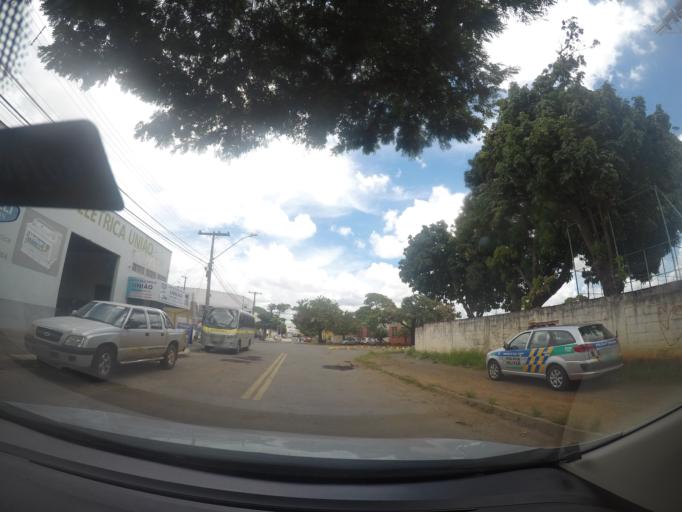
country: BR
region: Goias
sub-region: Goiania
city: Goiania
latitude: -16.6725
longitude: -49.3093
